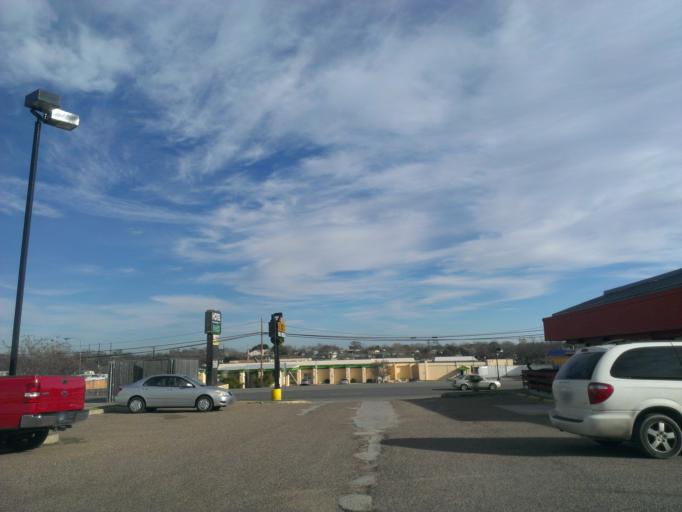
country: US
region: Texas
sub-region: Bell County
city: Killeen
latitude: 31.1110
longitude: -97.7475
